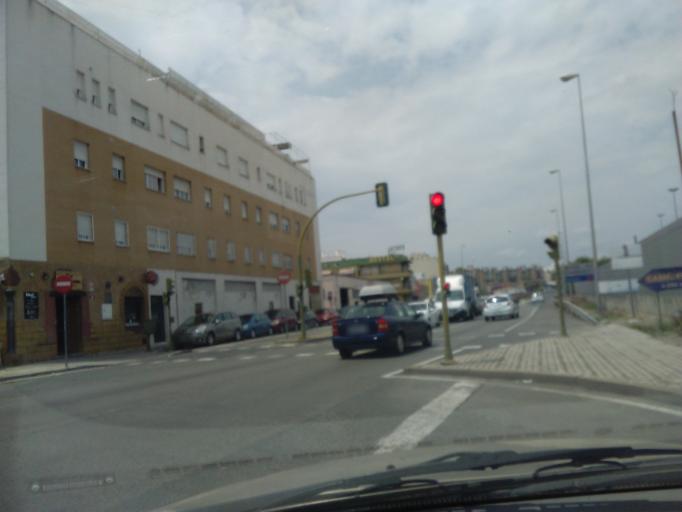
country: ES
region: Andalusia
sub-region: Provincia de Sevilla
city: Sevilla
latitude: 37.3816
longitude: -5.9390
